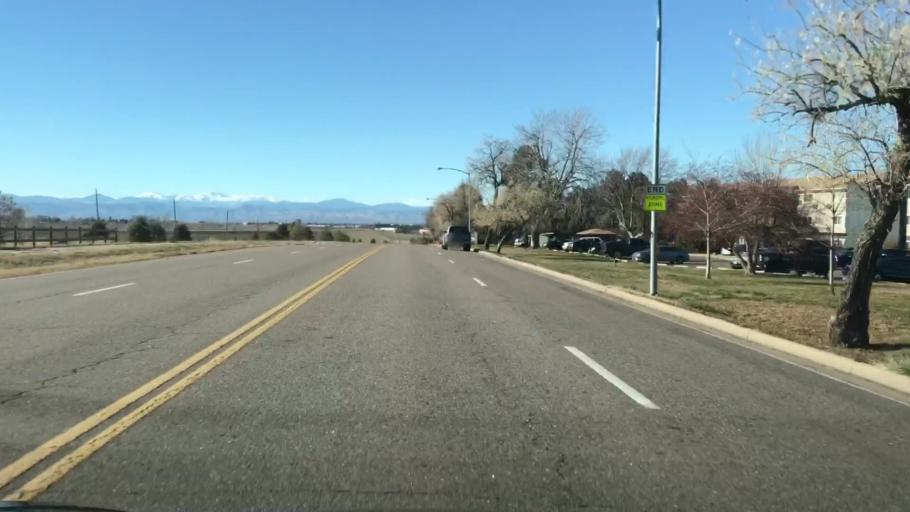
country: US
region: Colorado
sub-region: Adams County
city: Aurora
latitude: 39.7182
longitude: -104.8711
